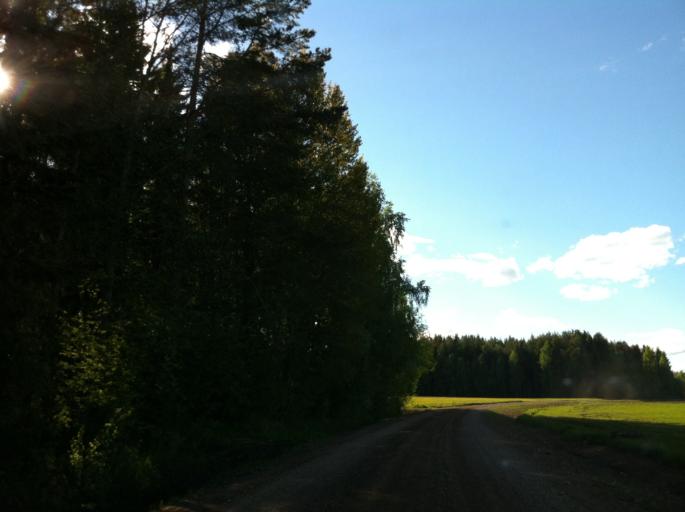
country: SE
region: Dalarna
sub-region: Leksand Municipality
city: Siljansnas
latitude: 60.7735
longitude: 14.8395
